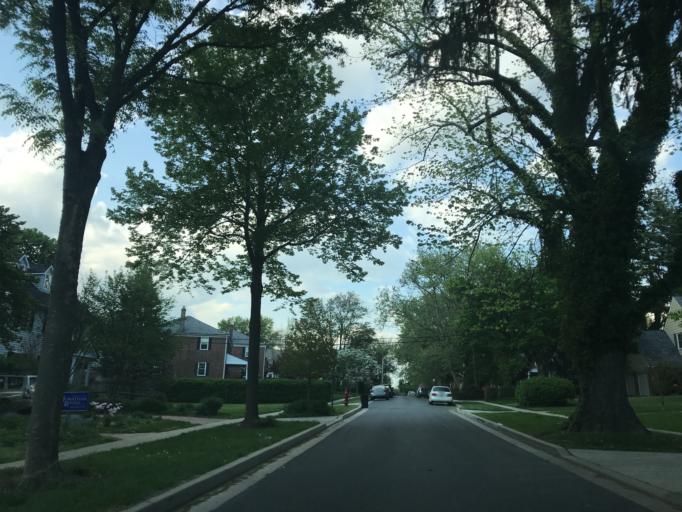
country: US
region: Maryland
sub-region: Baltimore County
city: Towson
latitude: 39.3747
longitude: -76.6148
